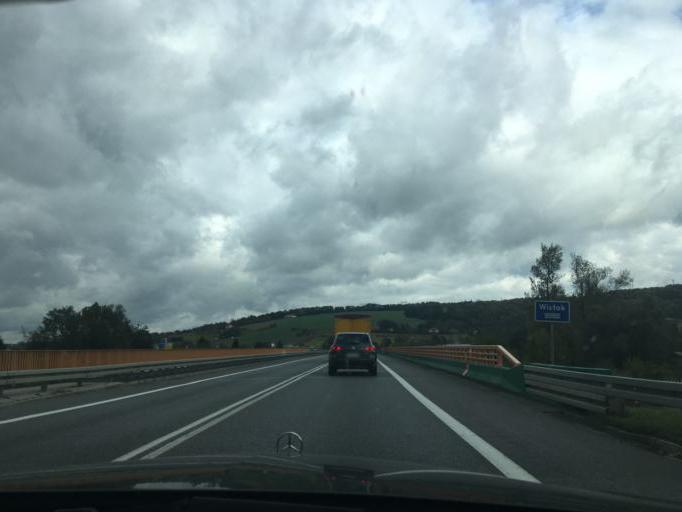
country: PL
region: Subcarpathian Voivodeship
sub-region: Powiat strzyzowski
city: Babica
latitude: 49.9290
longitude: 21.8730
